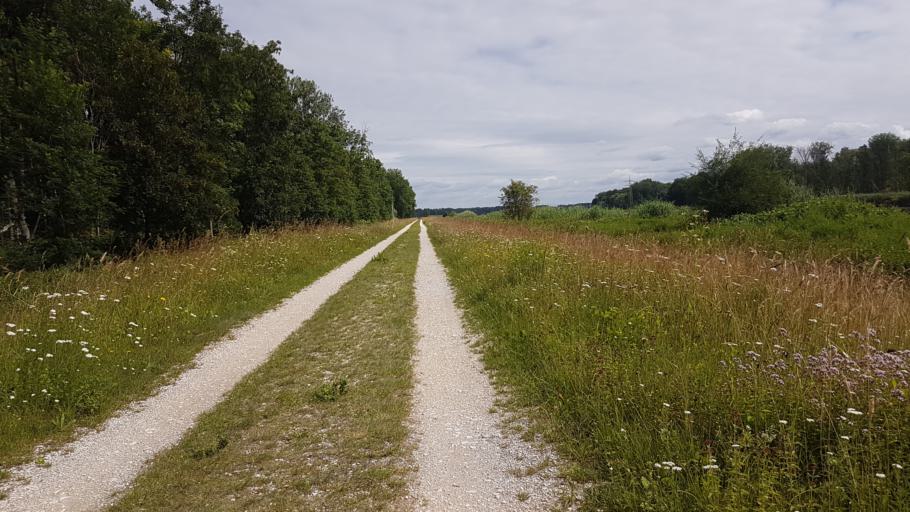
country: DE
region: Bavaria
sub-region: Swabia
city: Gundelfingen
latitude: 48.5384
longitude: 10.3922
